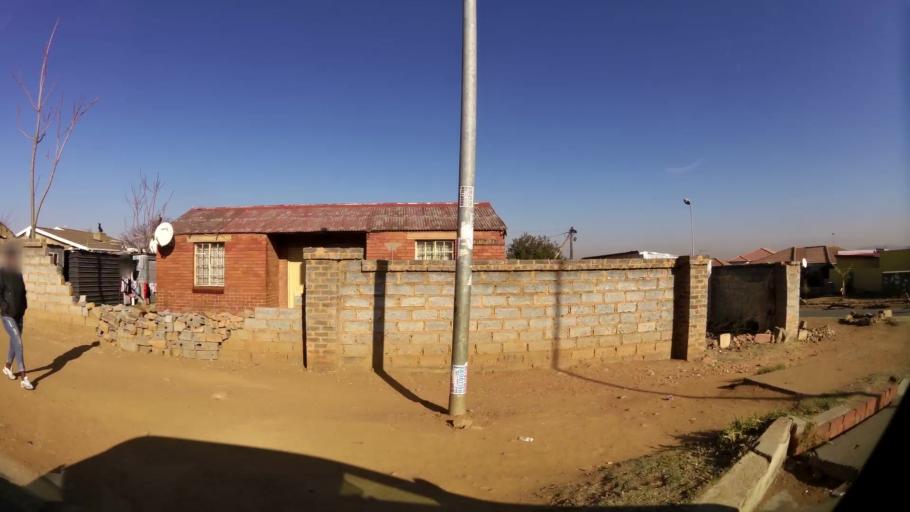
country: ZA
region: Gauteng
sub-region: City of Johannesburg Metropolitan Municipality
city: Soweto
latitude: -26.2340
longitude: 27.9328
